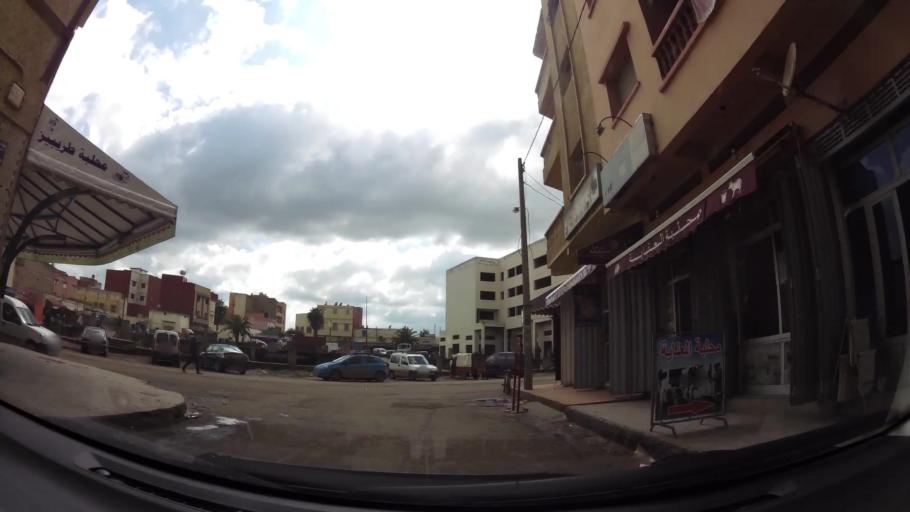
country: MA
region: Chaouia-Ouardigha
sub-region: Settat Province
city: Berrechid
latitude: 33.2657
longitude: -7.5874
